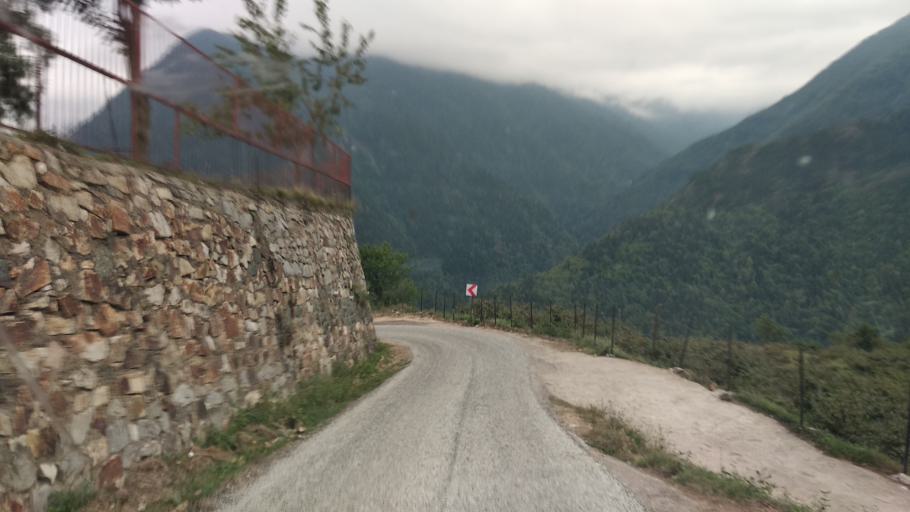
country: TR
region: Giresun
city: Dogankent
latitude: 40.7433
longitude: 38.9914
